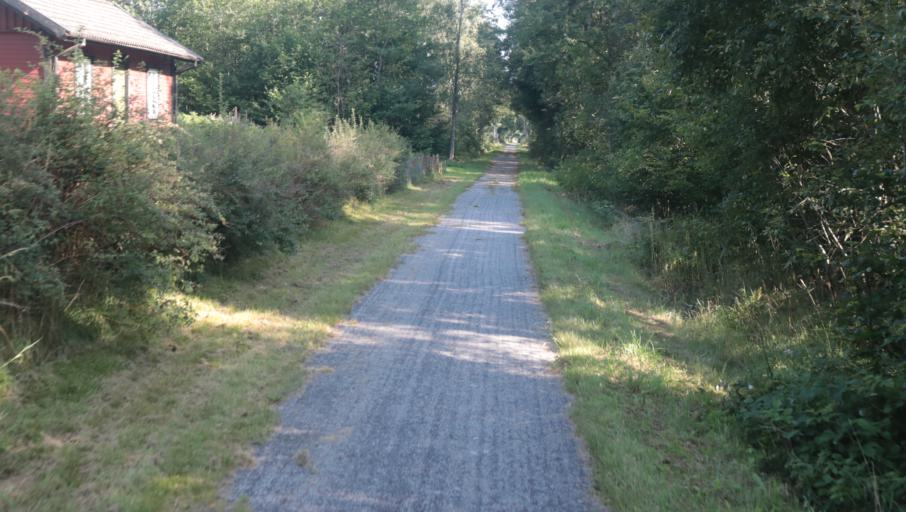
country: SE
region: Blekinge
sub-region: Karlshamns Kommun
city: Svangsta
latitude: 56.3065
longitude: 14.7251
